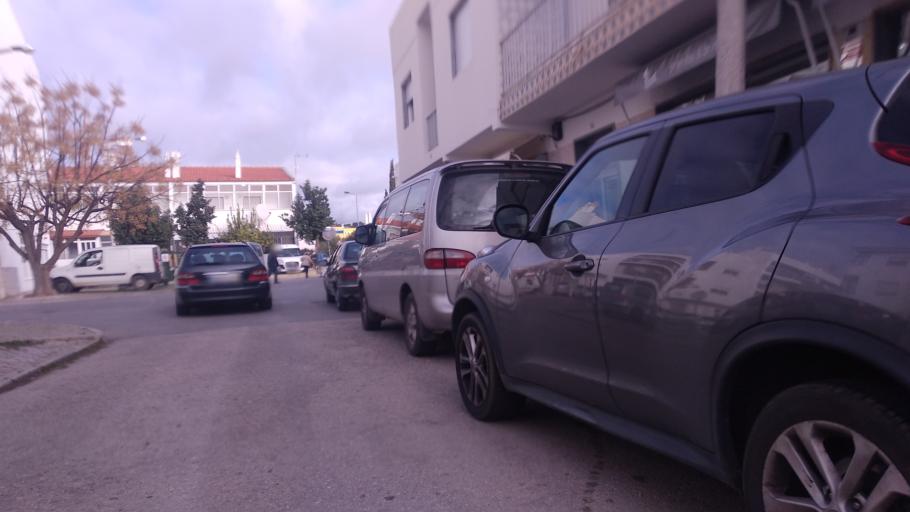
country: PT
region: Faro
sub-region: Sao Bras de Alportel
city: Sao Bras de Alportel
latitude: 37.1549
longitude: -7.8875
